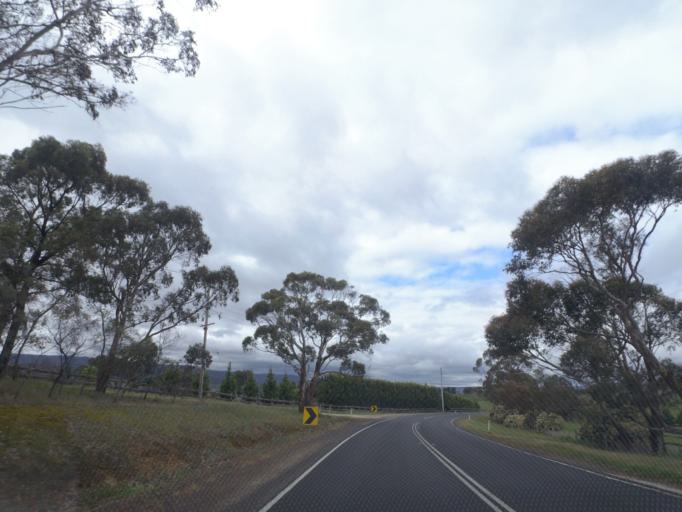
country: AU
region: Victoria
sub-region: Whittlesea
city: Whittlesea
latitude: -37.4969
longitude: 145.0901
